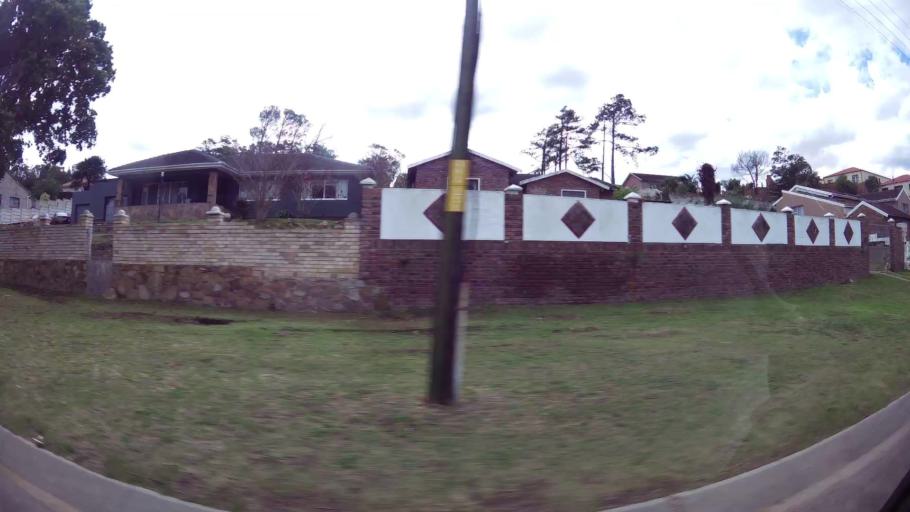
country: ZA
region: Eastern Cape
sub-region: Nelson Mandela Bay Metropolitan Municipality
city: Port Elizabeth
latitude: -33.9358
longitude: 25.5190
